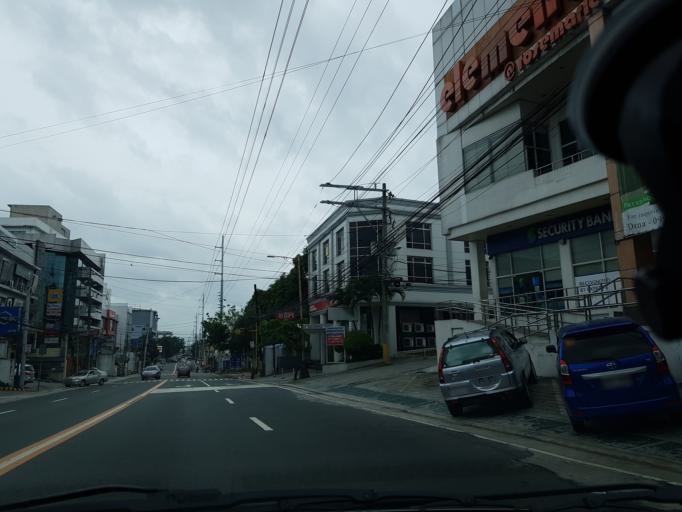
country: PH
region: Metro Manila
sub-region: Pasig
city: Pasig City
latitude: 14.5683
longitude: 121.0660
